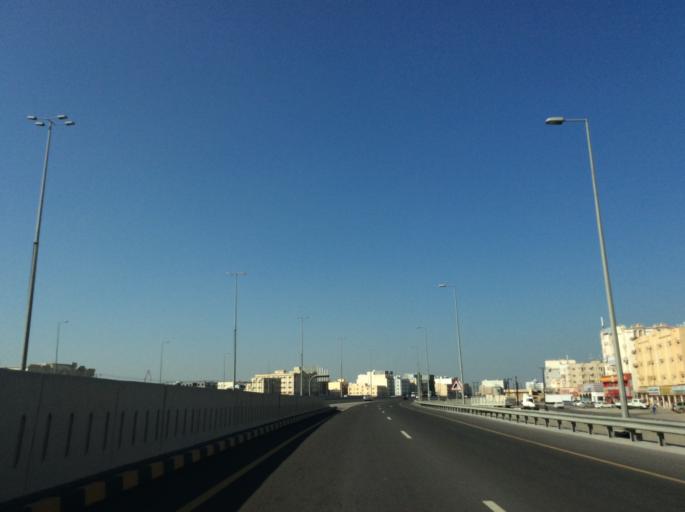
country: OM
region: Al Batinah
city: Al Liwa'
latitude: 24.4277
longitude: 56.6087
